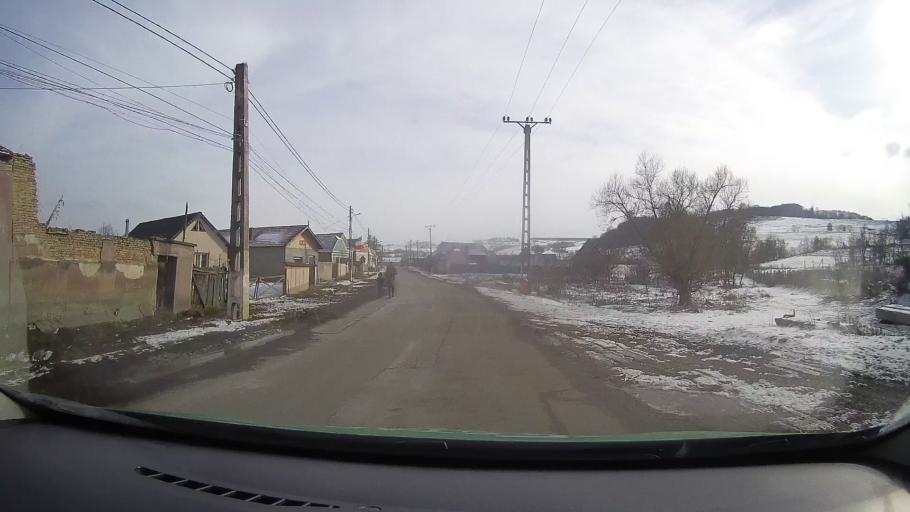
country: RO
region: Mures
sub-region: Comuna Apold
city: Apold
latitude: 46.1241
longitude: 24.8180
